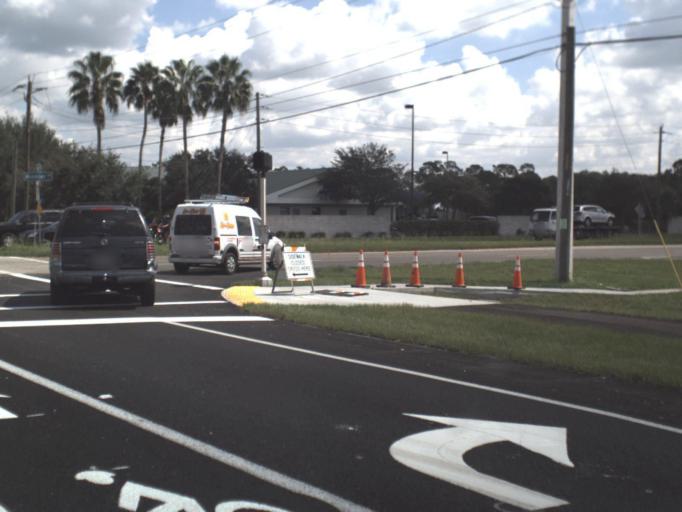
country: US
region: Florida
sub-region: Lee County
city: Fort Myers
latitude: 26.6094
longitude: -81.8215
